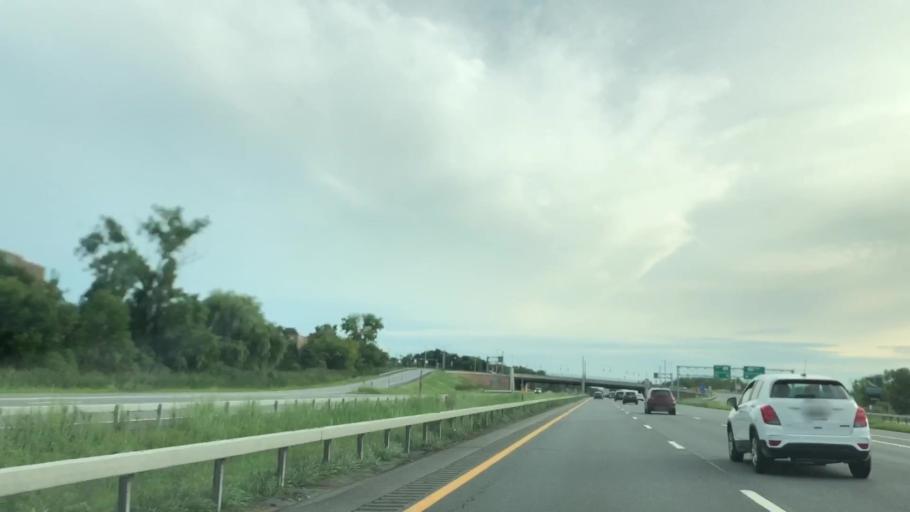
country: US
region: New York
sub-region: Albany County
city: Cohoes
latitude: 42.7569
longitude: -73.7674
